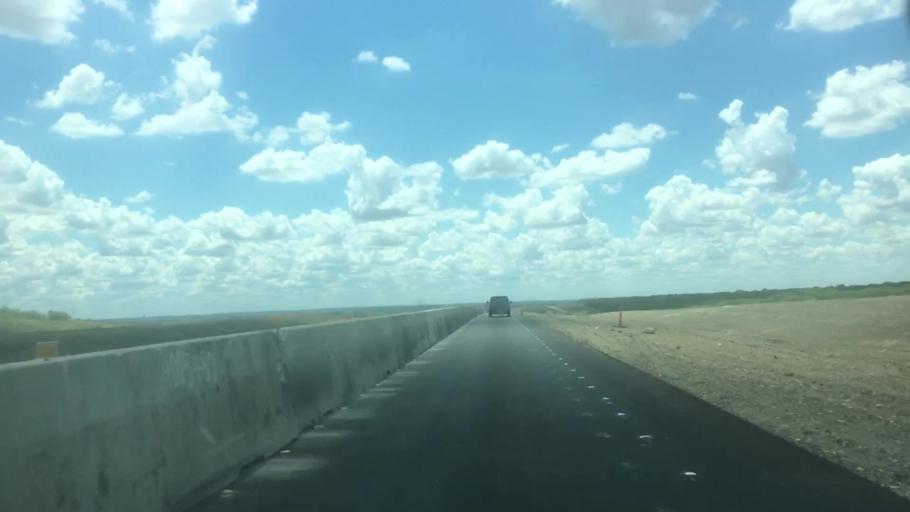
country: US
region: Texas
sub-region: Caldwell County
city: Martindale
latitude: 29.8139
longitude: -97.7635
